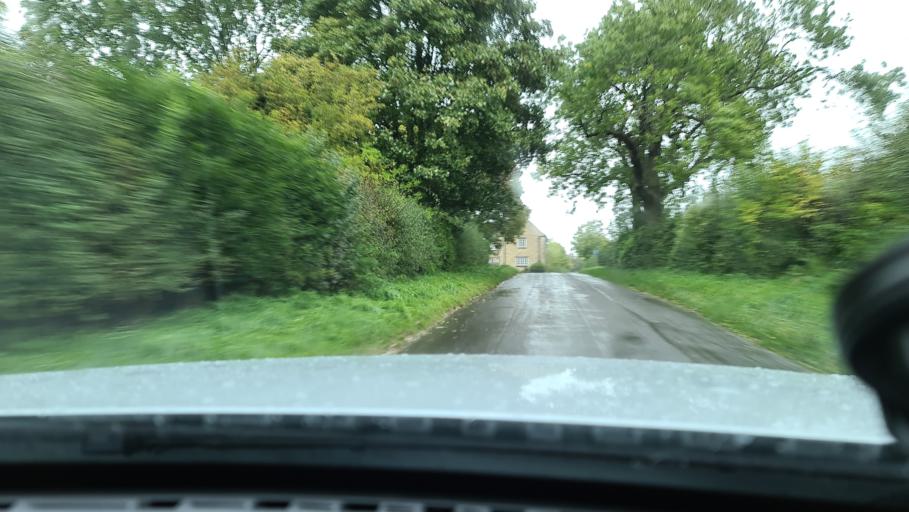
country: GB
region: England
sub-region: Oxfordshire
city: Woodstock
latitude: 51.8942
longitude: -1.3782
